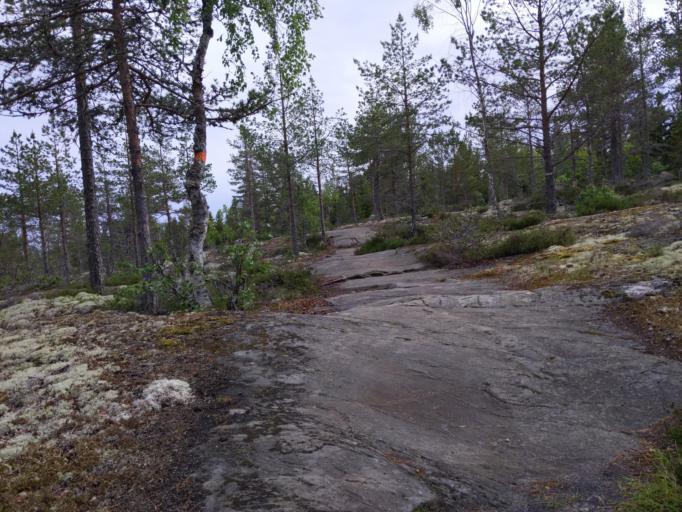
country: SE
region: Vaesternorrland
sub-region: OErnskoeldsviks Kommun
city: Ornskoldsvik
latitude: 63.1920
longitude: 18.6994
